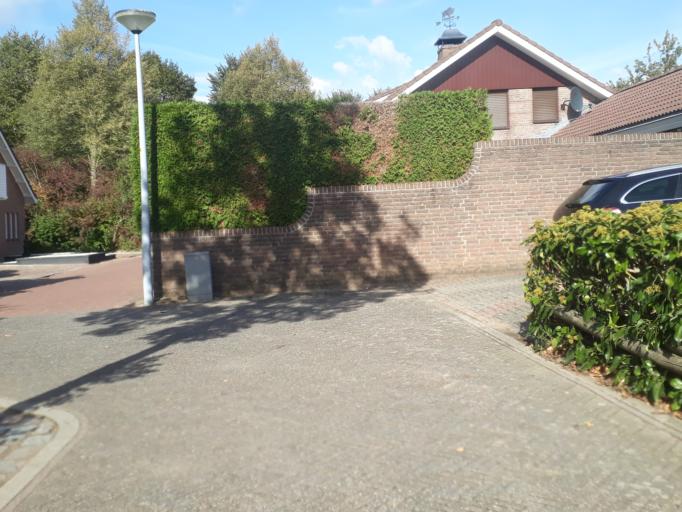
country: NL
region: Gelderland
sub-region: Gemeente Zevenaar
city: Zevenaar
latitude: 51.9336
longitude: 6.0522
